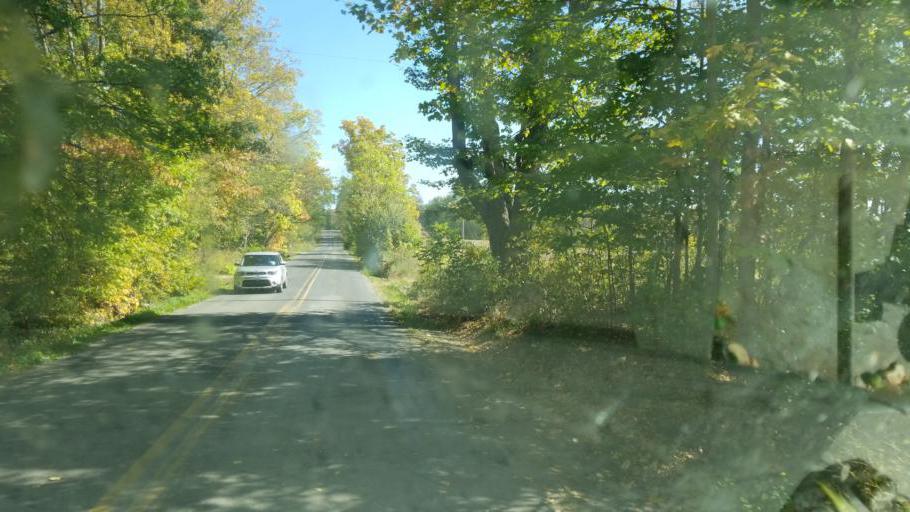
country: US
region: Pennsylvania
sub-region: Mercer County
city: Greenville
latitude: 41.3852
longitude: -80.4312
